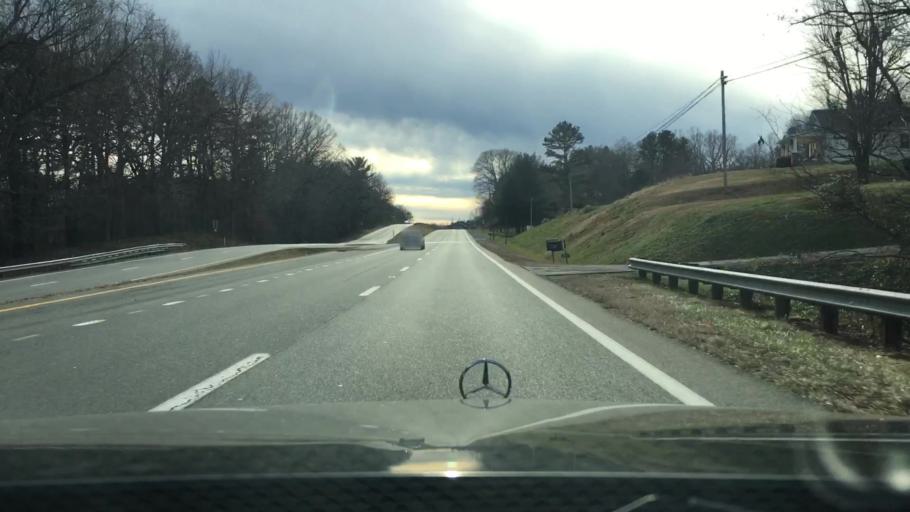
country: US
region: Virginia
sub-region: Pittsylvania County
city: Motley
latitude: 37.0547
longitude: -79.3531
